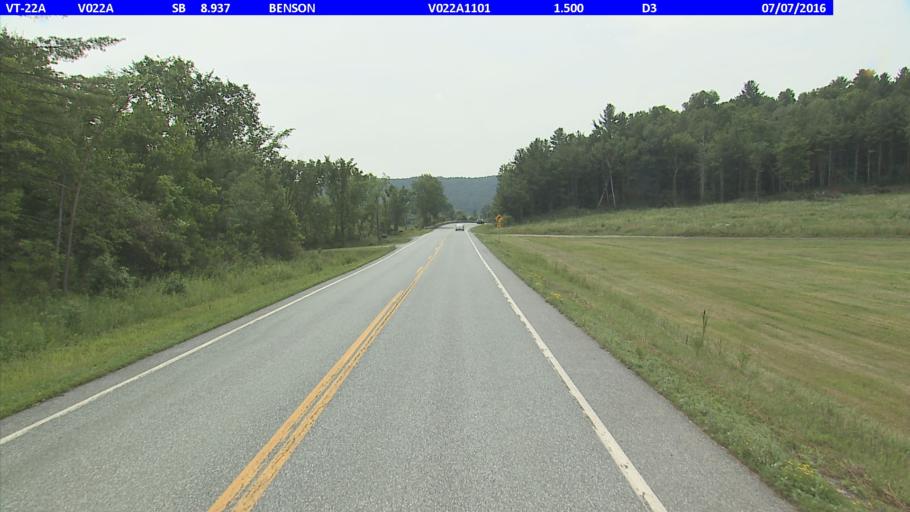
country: US
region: Vermont
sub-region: Rutland County
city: Fair Haven
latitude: 43.6905
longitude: -73.2915
